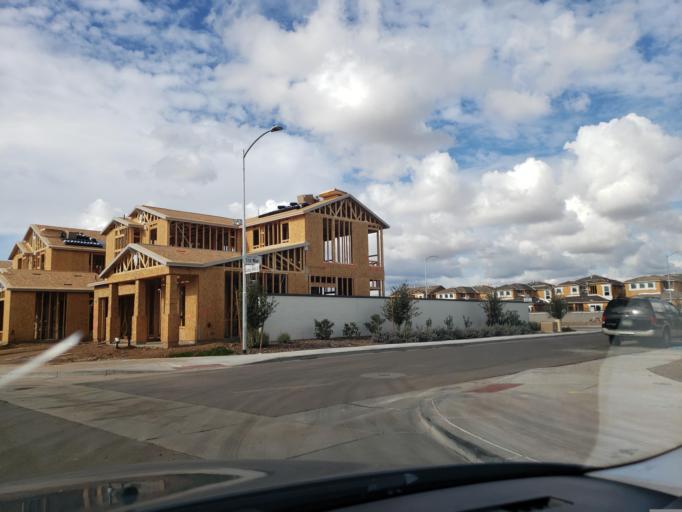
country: US
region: Arizona
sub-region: Maricopa County
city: Paradise Valley
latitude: 33.6440
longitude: -111.9693
